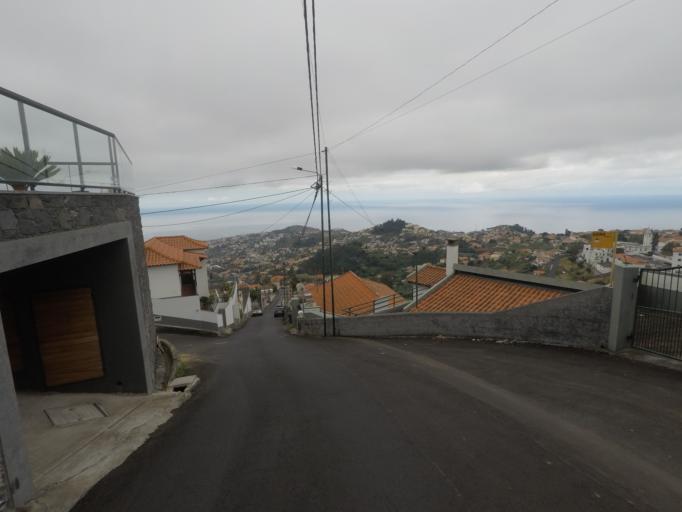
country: PT
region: Madeira
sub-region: Funchal
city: Nossa Senhora do Monte
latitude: 32.6799
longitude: -16.9433
